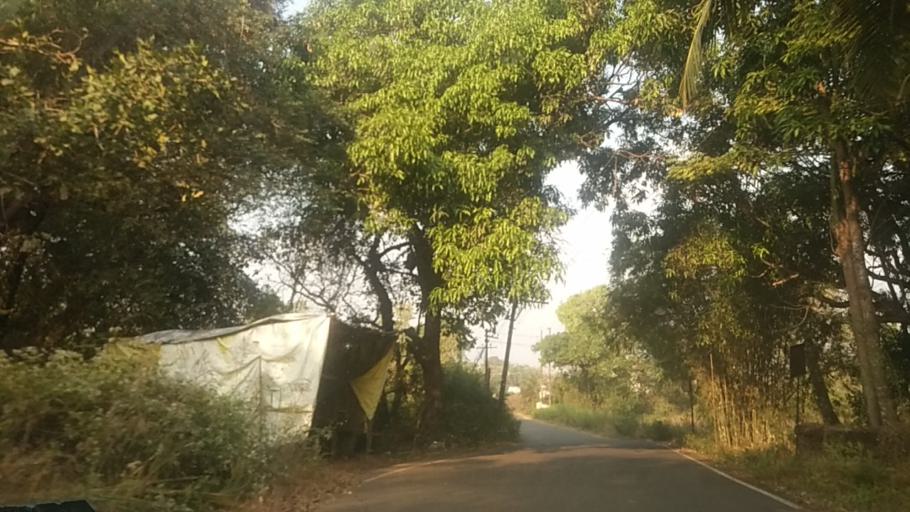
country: IN
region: Goa
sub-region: South Goa
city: Chinchinim
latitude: 15.2339
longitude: 73.9890
